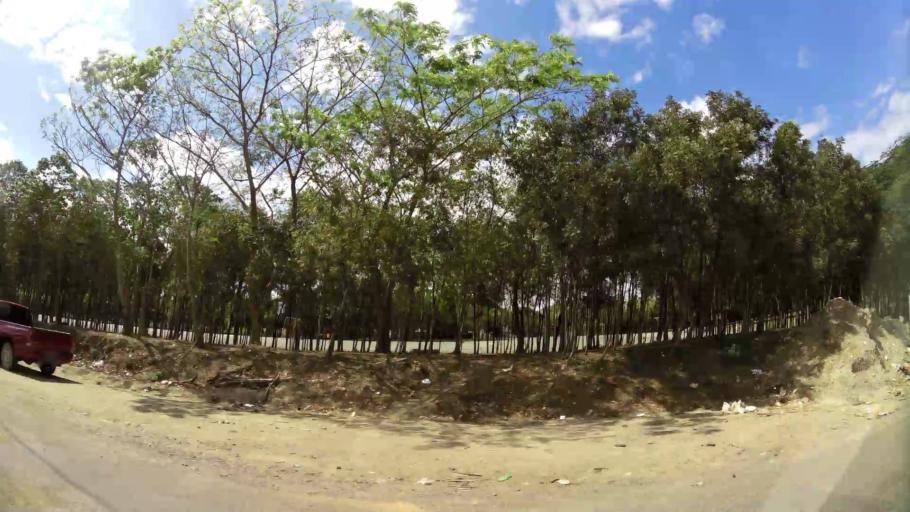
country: DO
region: Santiago
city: Santiago de los Caballeros
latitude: 19.4725
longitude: -70.7060
